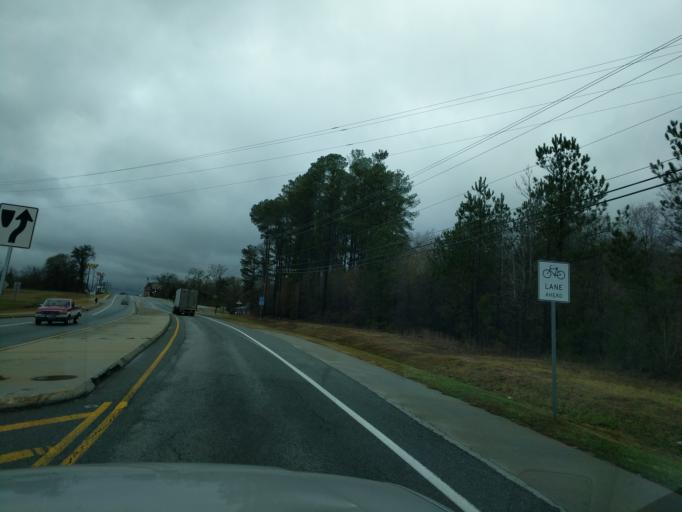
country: US
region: Georgia
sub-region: Franklin County
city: Lavonia
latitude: 34.4430
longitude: -83.1136
